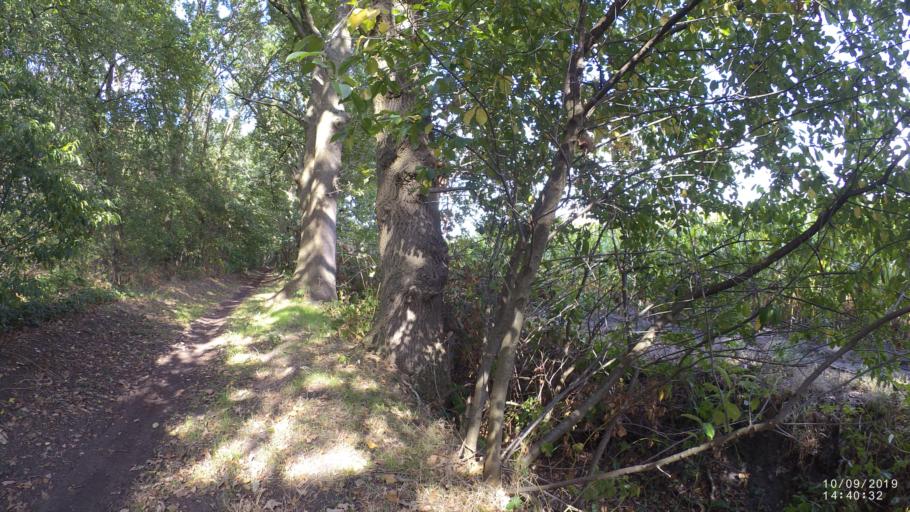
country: BE
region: Flanders
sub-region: Provincie Oost-Vlaanderen
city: Kaprijke
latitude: 51.1798
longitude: 3.6822
